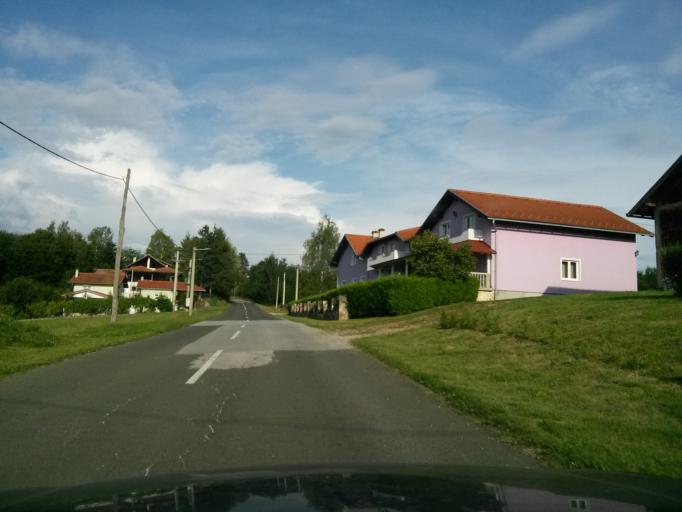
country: HR
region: Sisacko-Moslavacka
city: Gvozd
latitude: 45.5235
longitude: 15.8783
